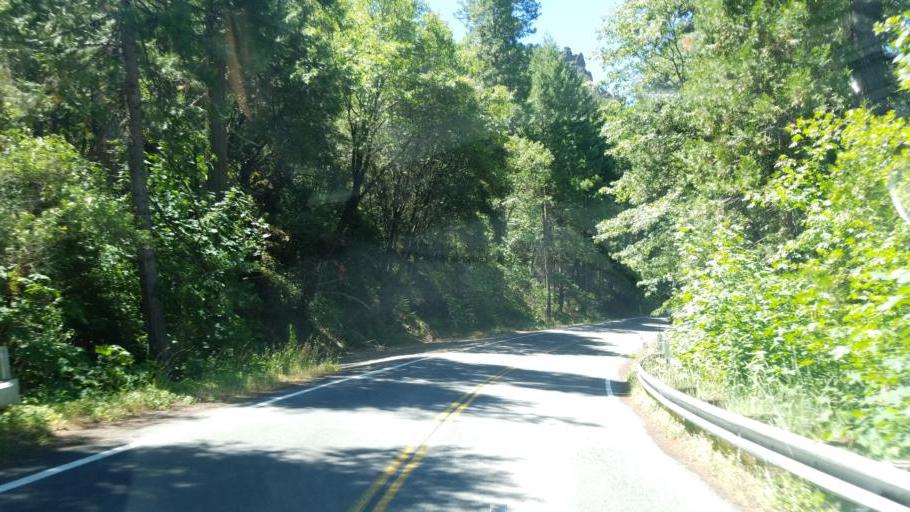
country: US
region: California
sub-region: Butte County
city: Forest Ranch
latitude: 40.1726
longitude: -121.5563
